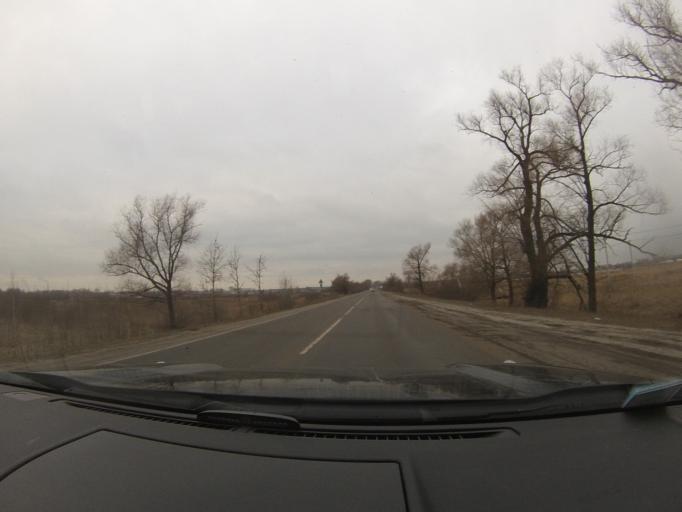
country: RU
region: Moskovskaya
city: Lopatinskiy
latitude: 55.3266
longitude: 38.7320
